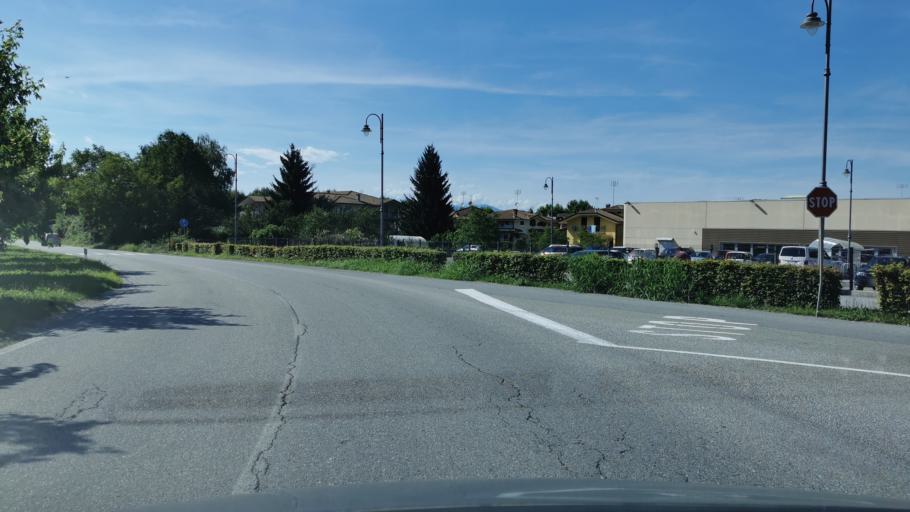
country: IT
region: Piedmont
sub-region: Provincia di Cuneo
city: Boves
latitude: 44.3326
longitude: 7.5577
